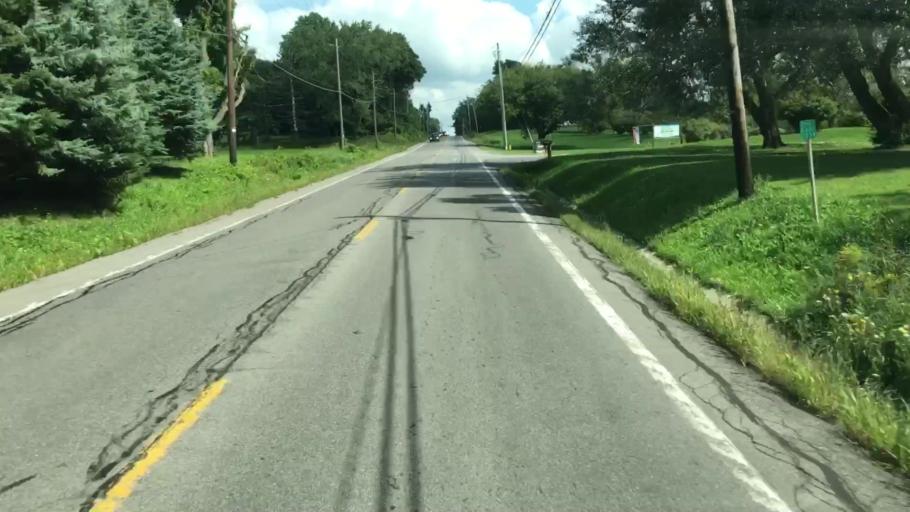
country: US
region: New York
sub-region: Onondaga County
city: Marcellus
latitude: 42.9835
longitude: -76.3148
